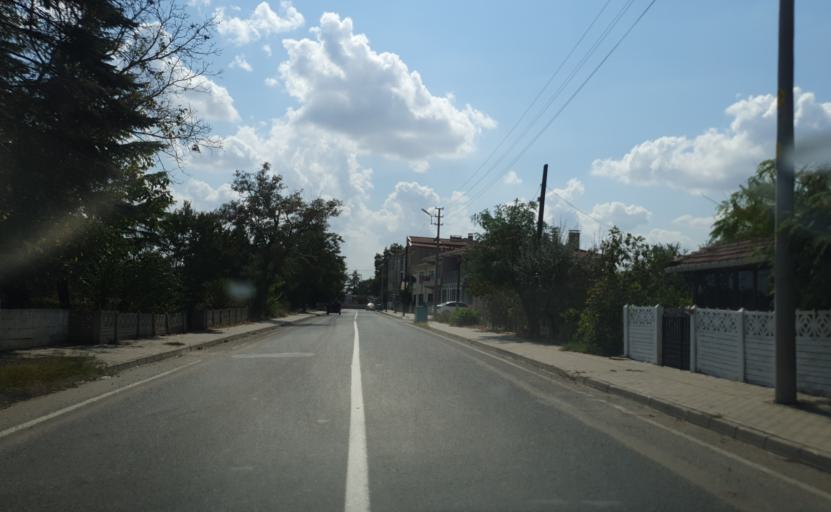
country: TR
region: Kirklareli
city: Luleburgaz
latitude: 41.3565
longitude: 27.3342
